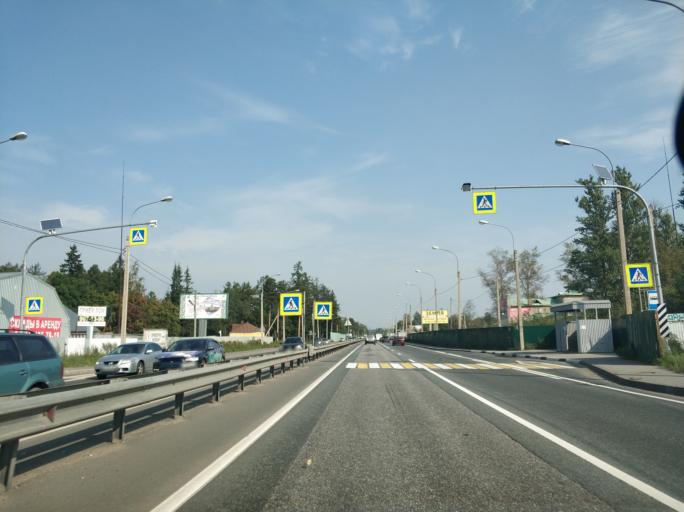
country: RU
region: Leningrad
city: Yanino Vtoroye
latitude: 60.0102
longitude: 30.5770
